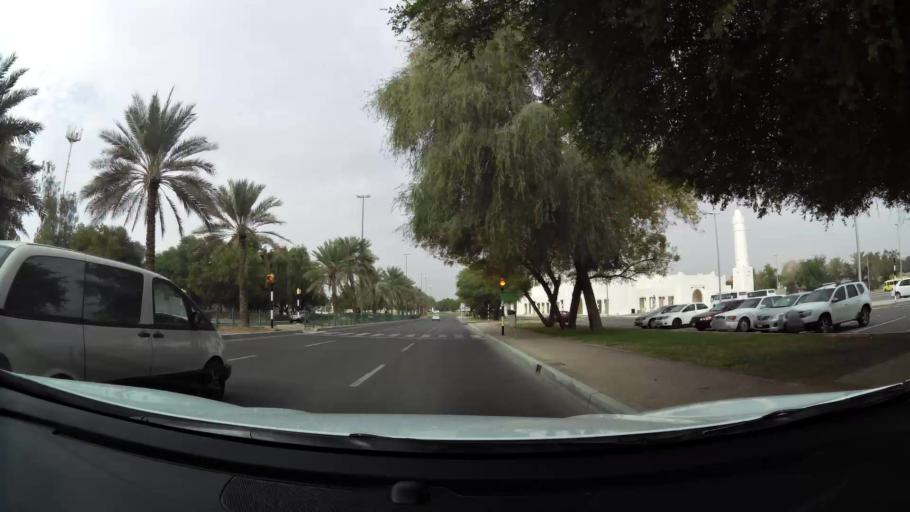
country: AE
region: Abu Dhabi
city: Al Ain
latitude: 24.2209
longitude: 55.7404
